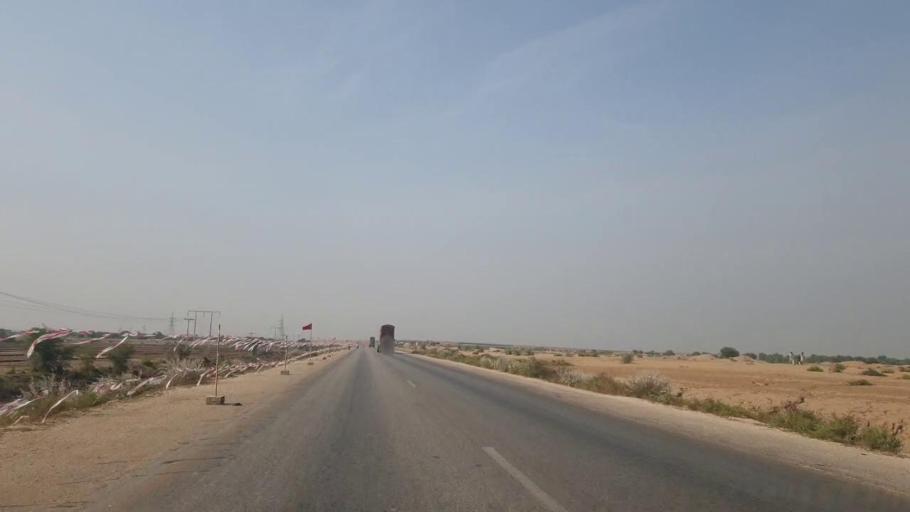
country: PK
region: Sindh
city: Sann
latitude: 26.1489
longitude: 68.0301
